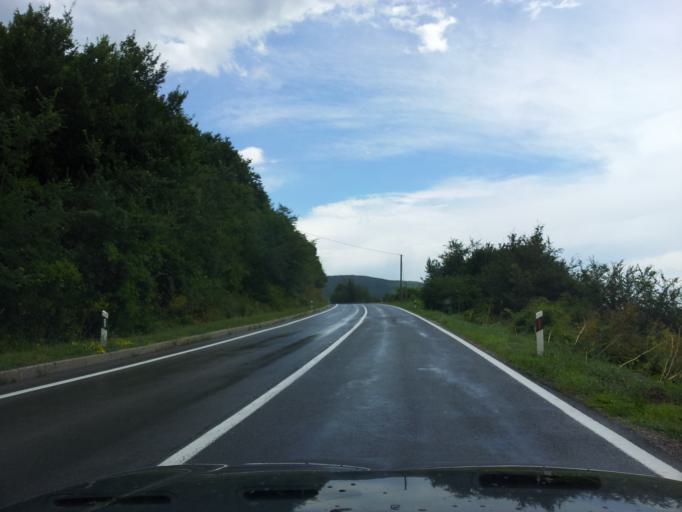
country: BA
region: Federation of Bosnia and Herzegovina
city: Bihac
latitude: 44.6381
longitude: 15.7217
